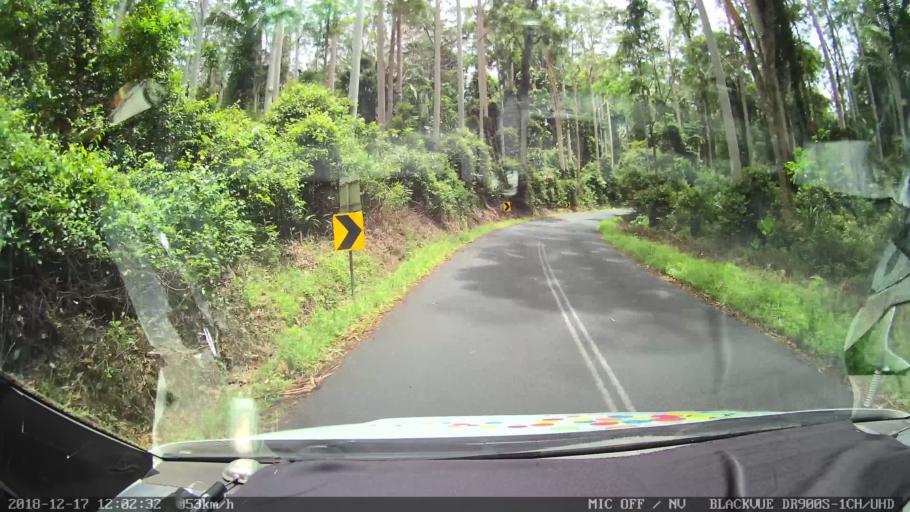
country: AU
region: New South Wales
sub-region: Kyogle
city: Kyogle
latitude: -28.5152
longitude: 152.5684
